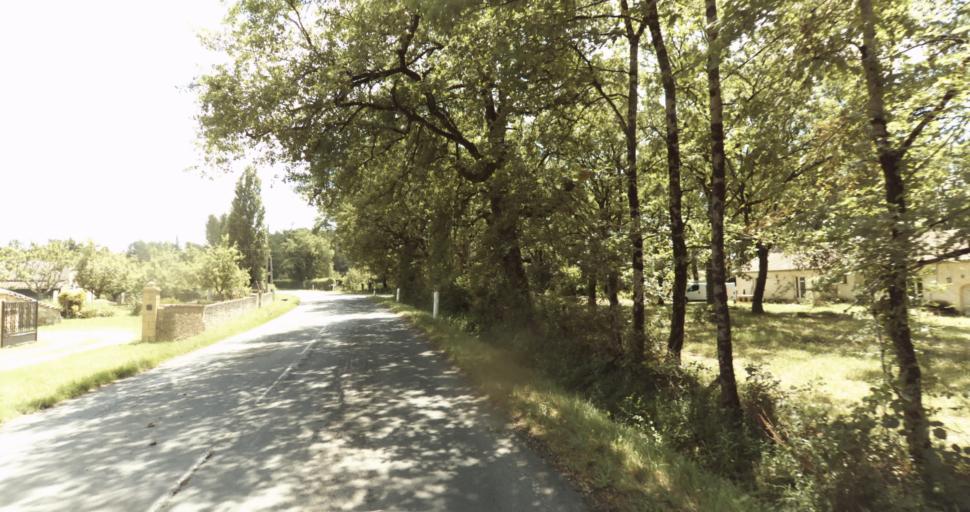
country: FR
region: Aquitaine
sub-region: Departement de la Dordogne
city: Beaumont-du-Perigord
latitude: 44.7498
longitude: 0.7752
